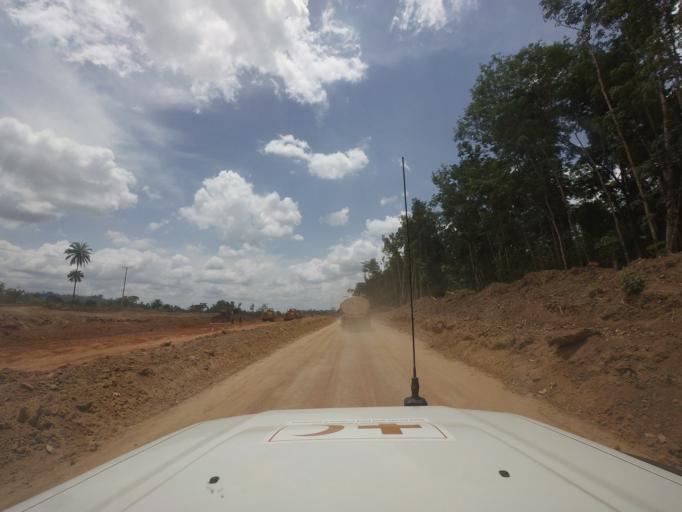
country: LR
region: Nimba
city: Sanniquellie
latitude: 7.2457
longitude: -8.8657
